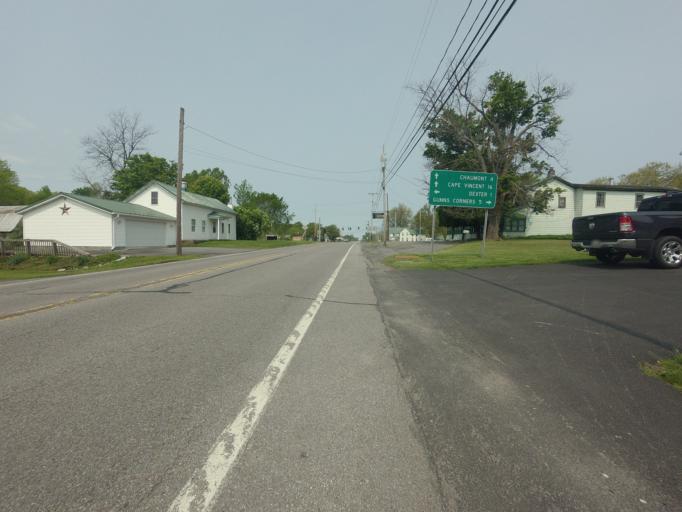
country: US
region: New York
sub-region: Jefferson County
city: Dexter
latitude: 44.0286
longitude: -76.0460
